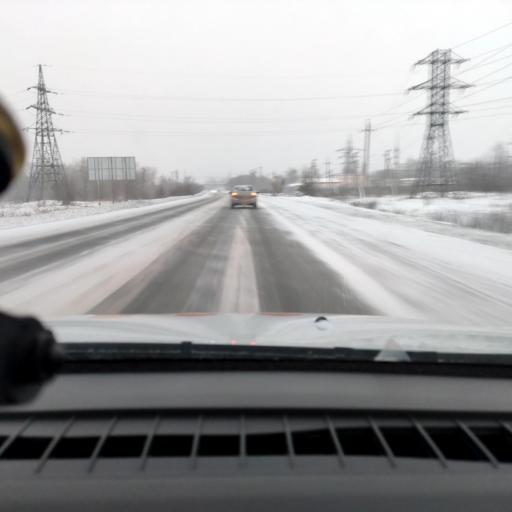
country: RU
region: Samara
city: Otradnyy
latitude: 53.3486
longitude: 51.3183
